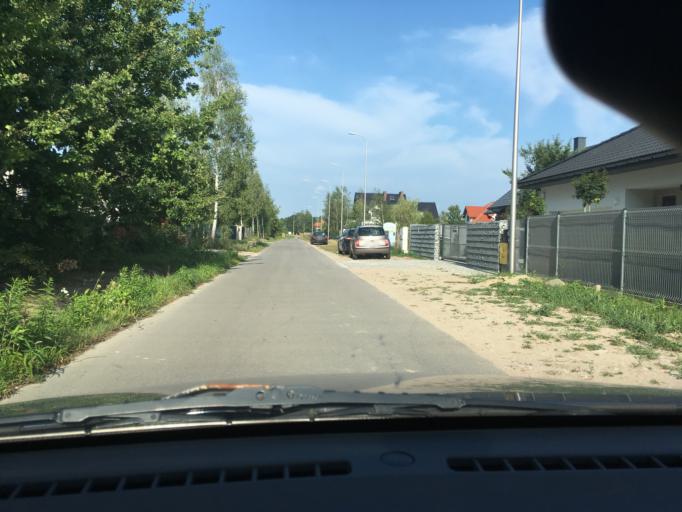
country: PL
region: Masovian Voivodeship
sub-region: Powiat piaseczynski
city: Lesznowola
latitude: 52.0515
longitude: 20.9365
